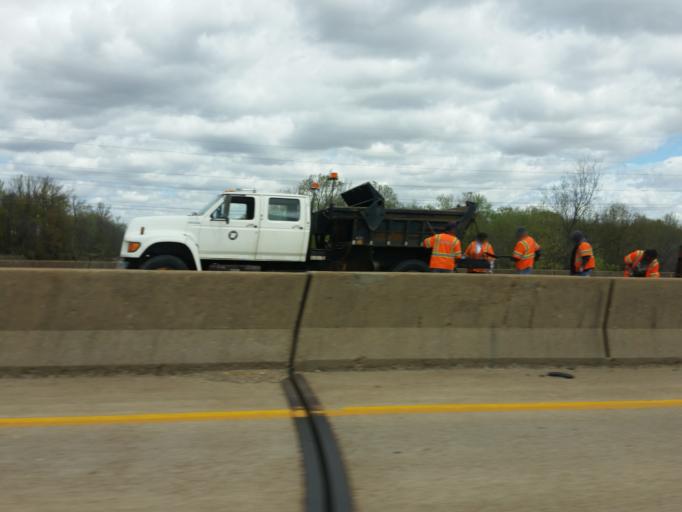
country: US
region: Arkansas
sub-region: Poinsett County
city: Marked Tree
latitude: 35.5379
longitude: -90.4854
